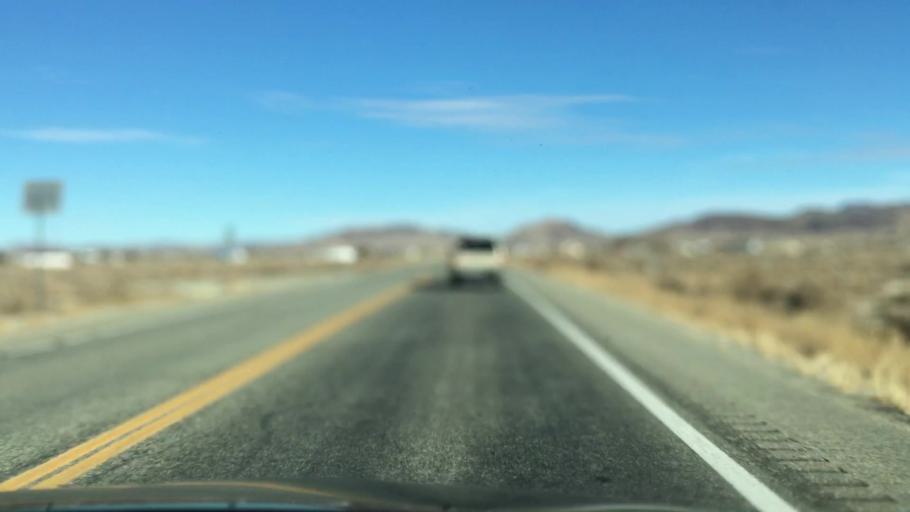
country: US
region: Nevada
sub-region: Lyon County
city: Yerington
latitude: 39.0068
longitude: -119.0846
